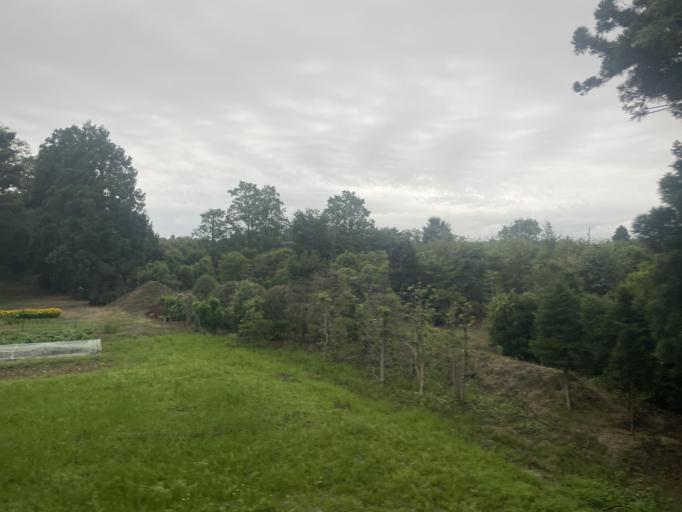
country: JP
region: Akita
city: Tenno
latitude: 39.8281
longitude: 140.0466
